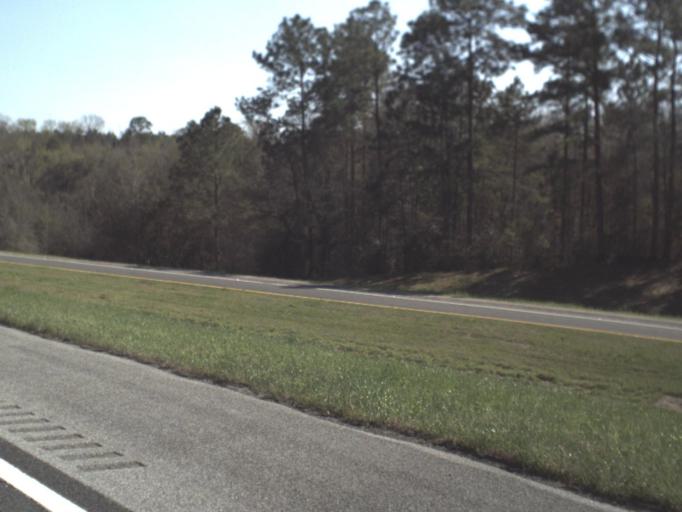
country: US
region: Florida
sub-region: Jackson County
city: Sneads
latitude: 30.6557
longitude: -85.0359
